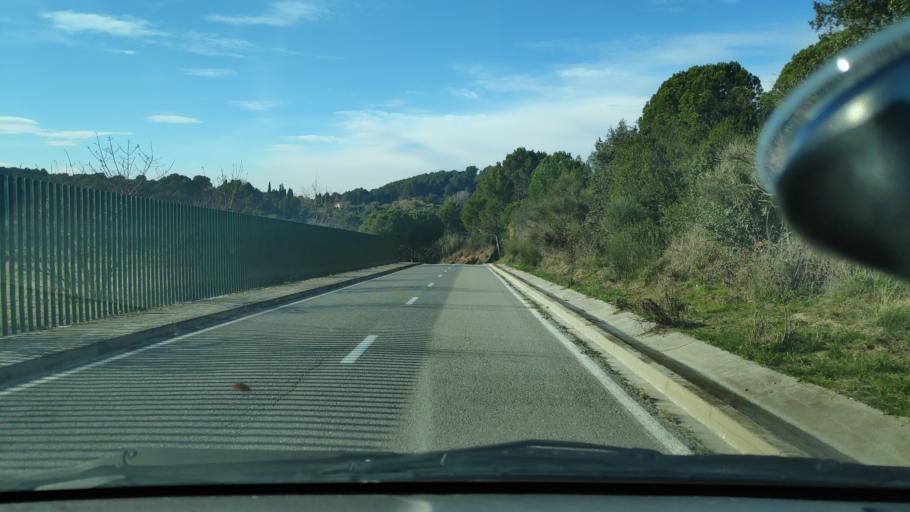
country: ES
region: Catalonia
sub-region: Provincia de Barcelona
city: Rubi
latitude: 41.4977
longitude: 2.0629
